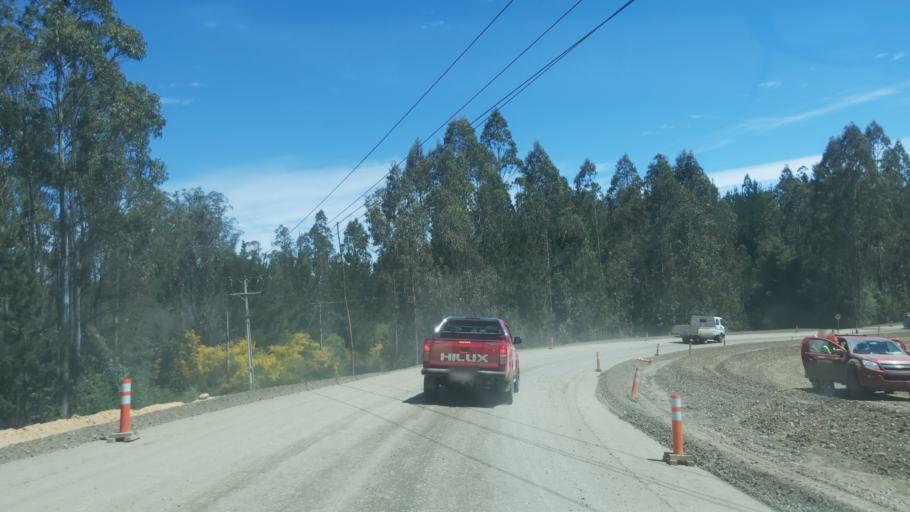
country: CL
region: Maule
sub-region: Provincia de Talca
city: Constitucion
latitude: -35.3865
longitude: -72.4198
